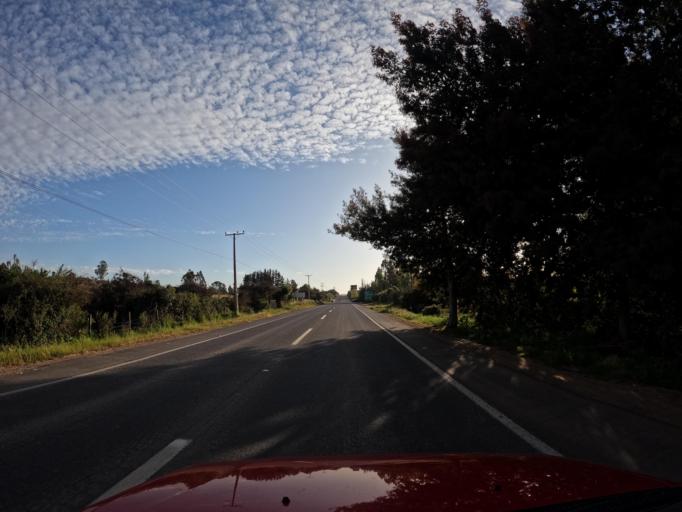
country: CL
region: Valparaiso
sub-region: San Antonio Province
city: San Antonio
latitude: -34.1002
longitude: -71.6986
